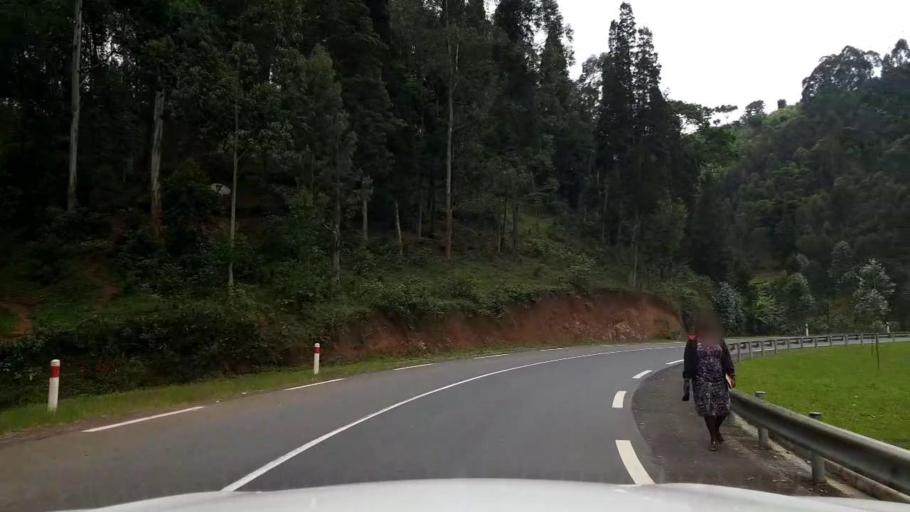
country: RW
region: Western Province
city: Kibuye
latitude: -1.9198
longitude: 29.3699
